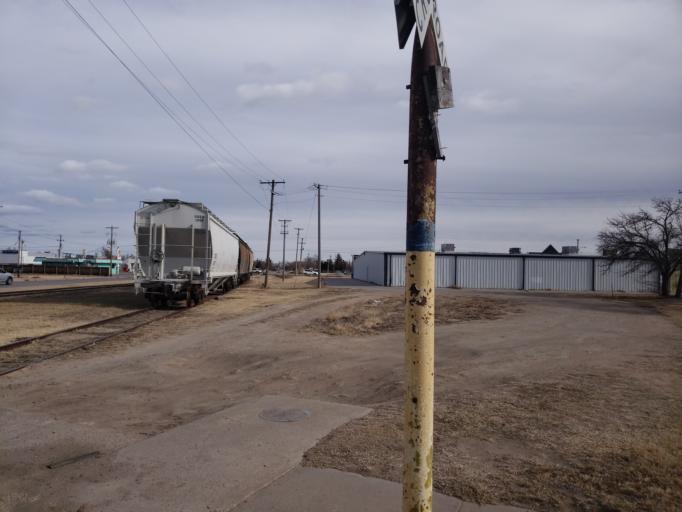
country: US
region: Kansas
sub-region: Ford County
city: Dodge City
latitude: 37.7419
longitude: -100.0213
